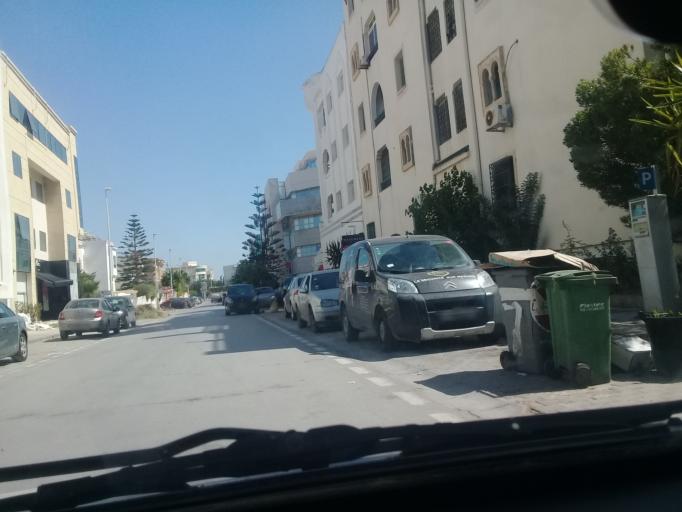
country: TN
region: Ariana
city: Ariana
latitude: 36.8404
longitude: 10.2455
